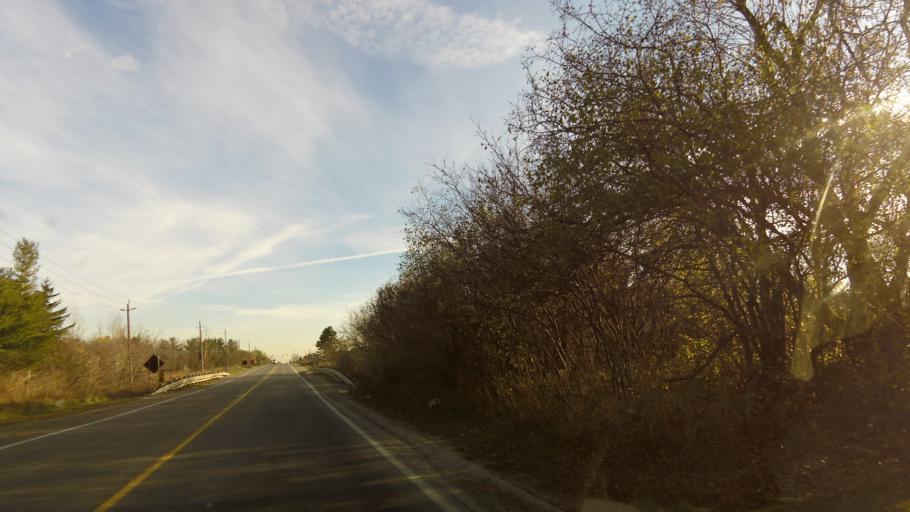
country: CA
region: Ontario
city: Brampton
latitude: 43.7902
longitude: -79.7347
